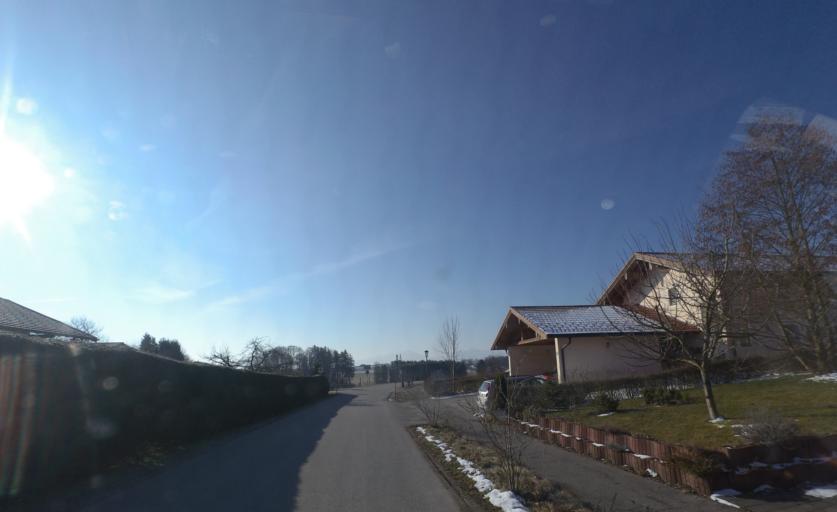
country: DE
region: Bavaria
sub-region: Upper Bavaria
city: Seeon-Seebruck
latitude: 47.9331
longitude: 12.5023
